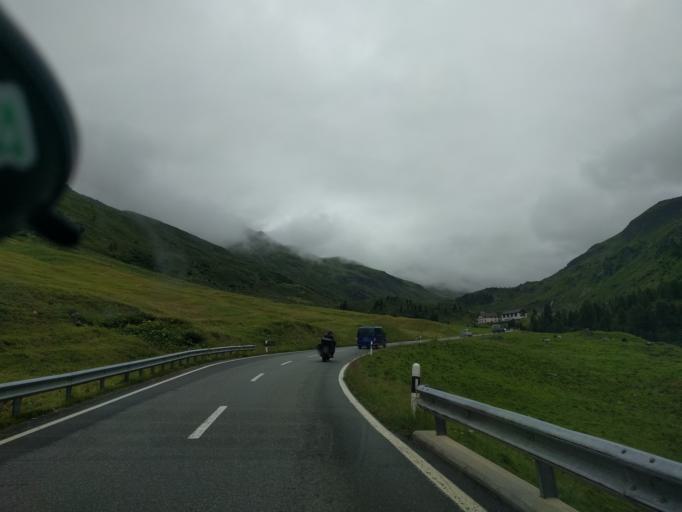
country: CH
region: Grisons
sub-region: Praettigau/Davos District
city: Davos
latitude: 46.7908
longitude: 9.9156
